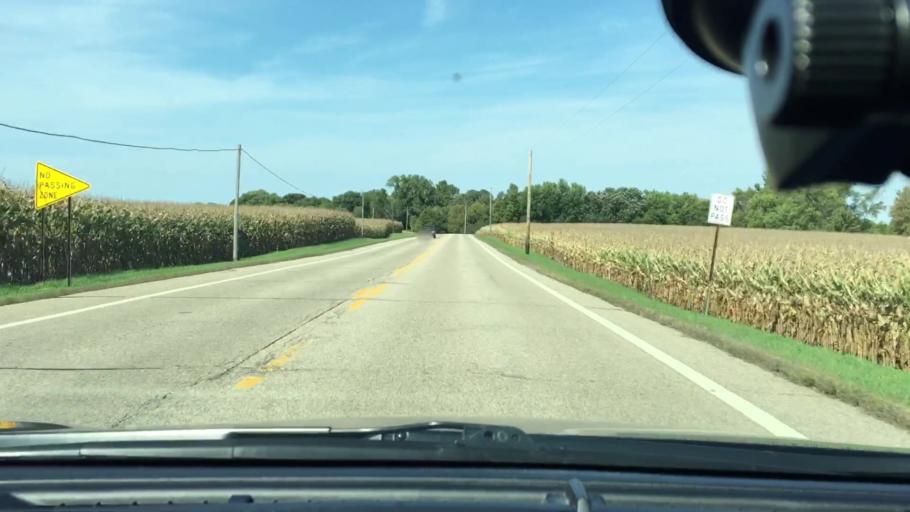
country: US
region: Minnesota
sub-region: Hennepin County
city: Corcoran
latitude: 45.1100
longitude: -93.5670
